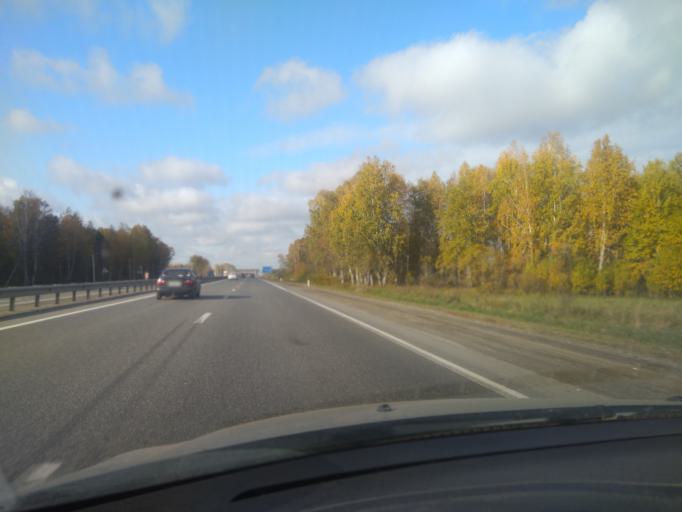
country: RU
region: Tjumen
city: Moskovskiy
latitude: 57.1034
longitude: 65.3281
